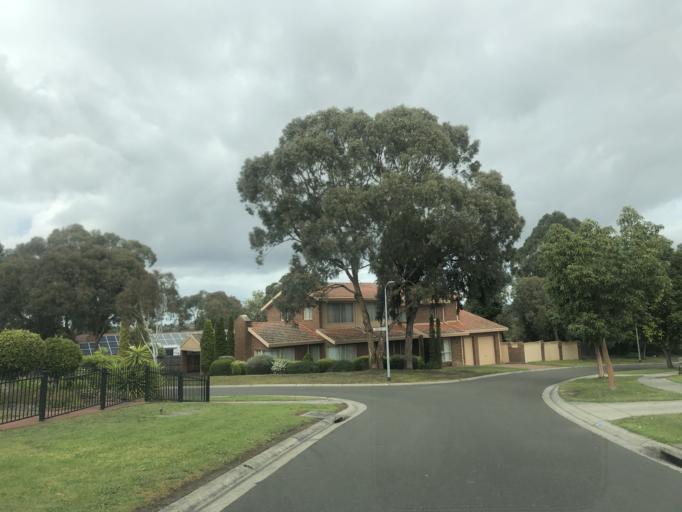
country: AU
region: Victoria
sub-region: Knox
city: Rowville
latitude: -37.9365
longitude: 145.2295
